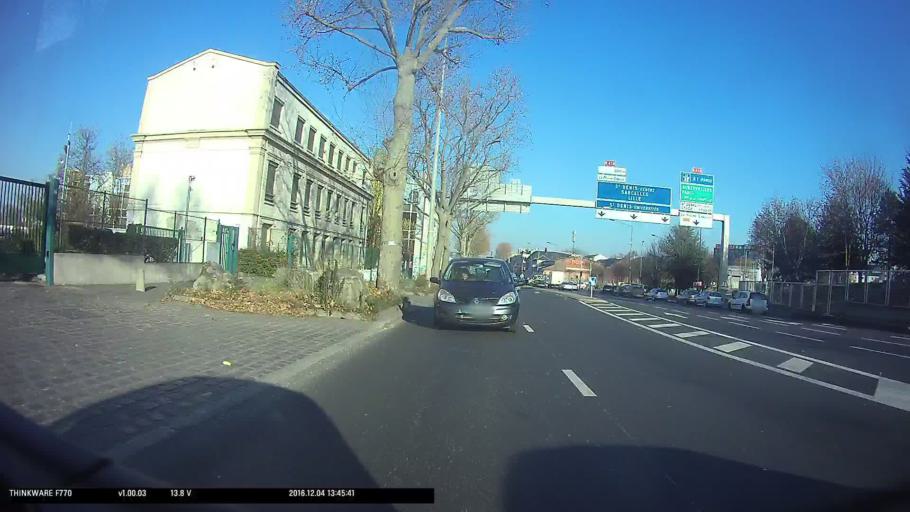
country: FR
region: Ile-de-France
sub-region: Departement de Seine-Saint-Denis
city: Saint-Denis
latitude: 48.9249
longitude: 2.3496
